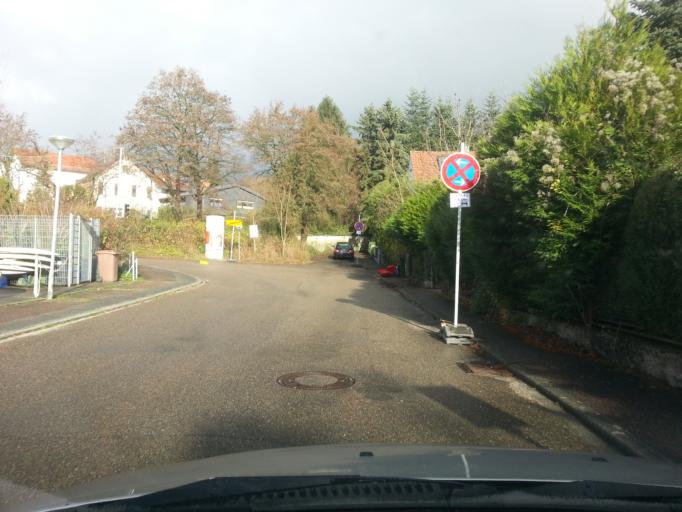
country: DE
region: Baden-Wuerttemberg
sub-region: Karlsruhe Region
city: Wiesloch
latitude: 49.2997
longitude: 8.7169
